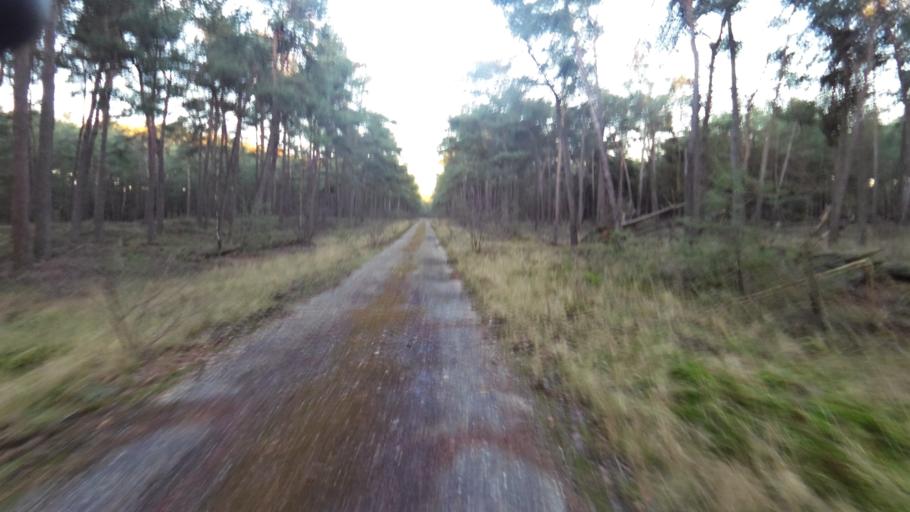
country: NL
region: Gelderland
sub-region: Gemeente Apeldoorn
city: Uddel
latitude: 52.1985
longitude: 5.7917
